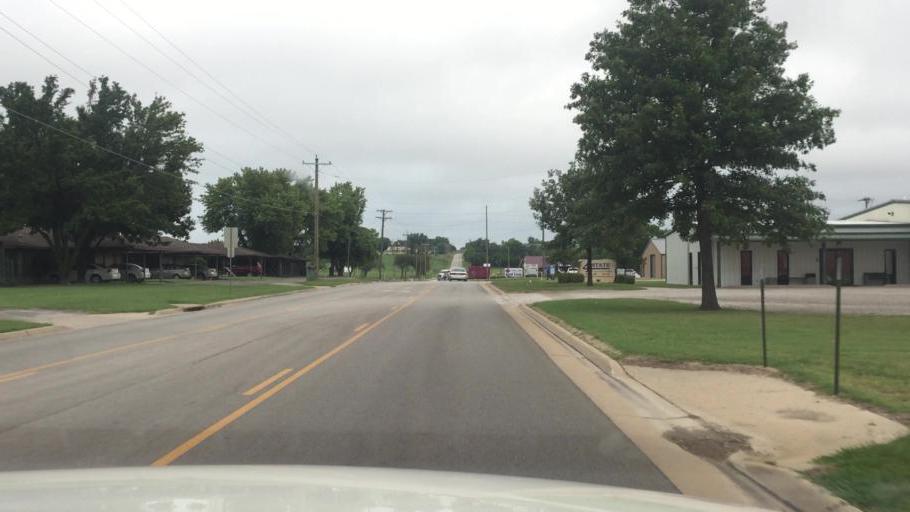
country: US
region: Kansas
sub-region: Montgomery County
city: Coffeyville
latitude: 37.0483
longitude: -95.6473
